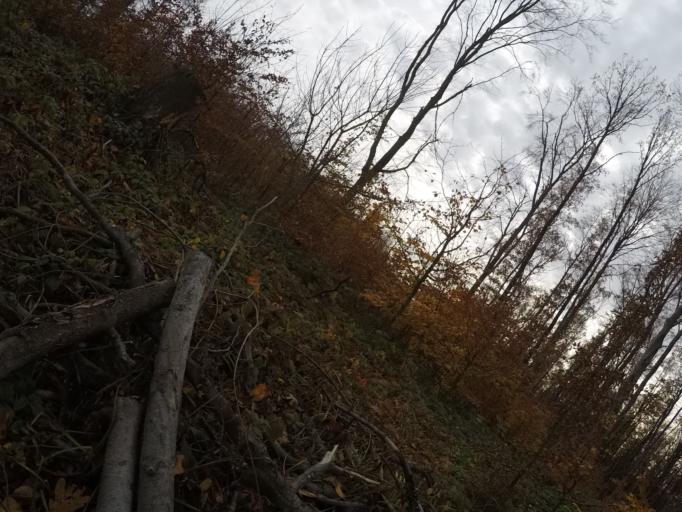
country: SK
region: Presovsky
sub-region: Okres Presov
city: Presov
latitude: 48.9699
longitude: 21.2123
